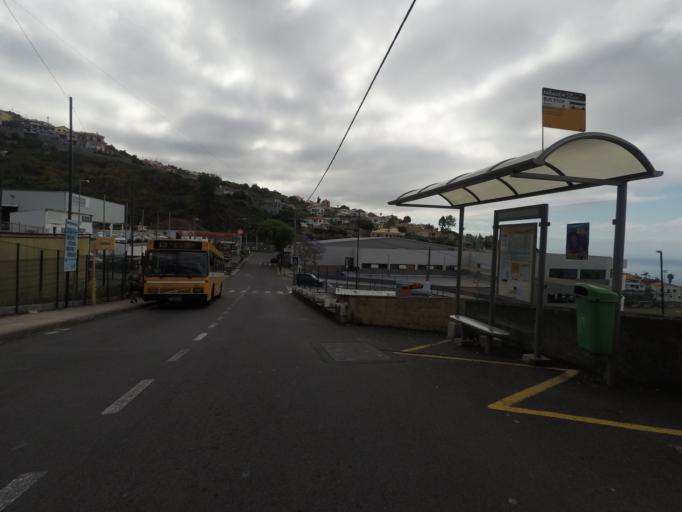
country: PT
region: Madeira
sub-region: Funchal
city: Nossa Senhora do Monte
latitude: 32.6719
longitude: -16.9364
